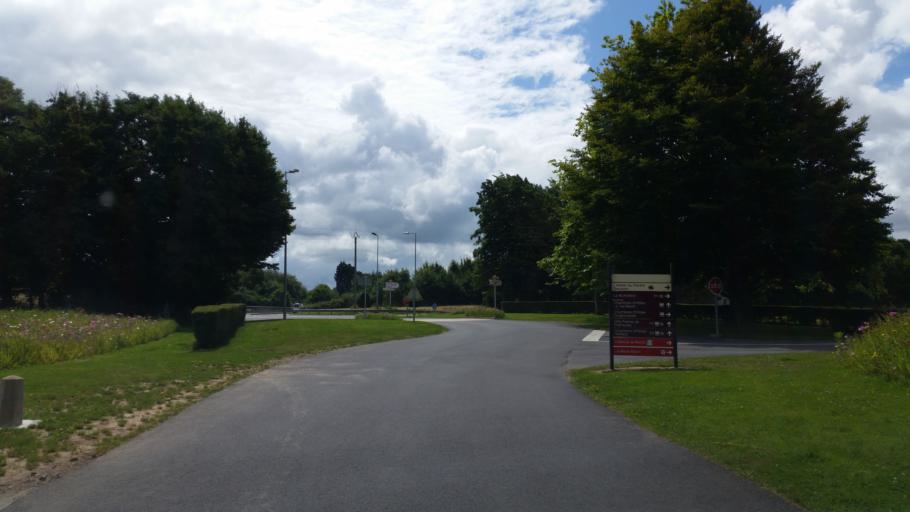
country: FR
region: Lower Normandy
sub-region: Departement du Calvados
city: La Riviere-Saint-Sauveur
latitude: 49.3829
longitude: 0.2445
